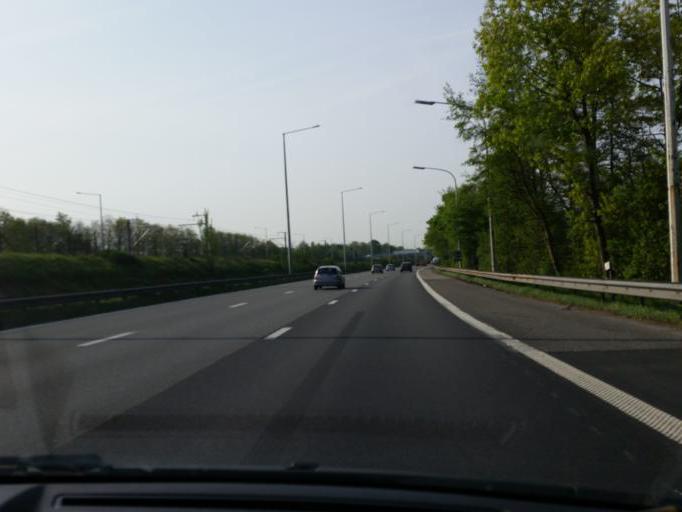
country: BE
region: Flanders
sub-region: Provincie Vlaams-Brabant
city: Zemst
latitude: 50.9687
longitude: 4.4905
